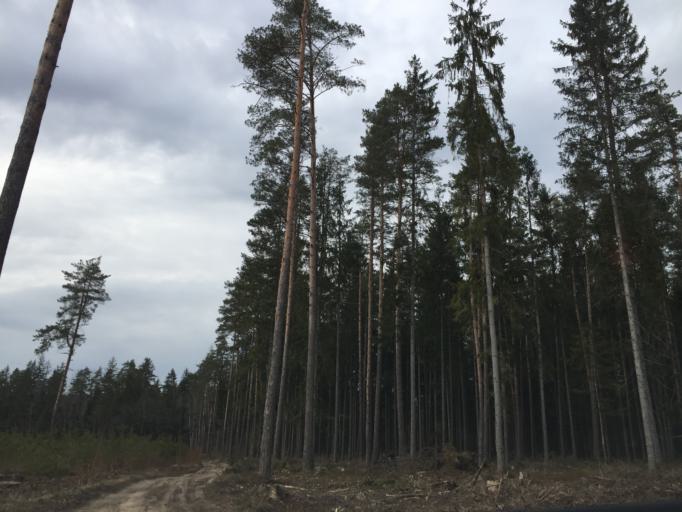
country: LV
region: Sigulda
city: Sigulda
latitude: 57.1324
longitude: 24.8029
